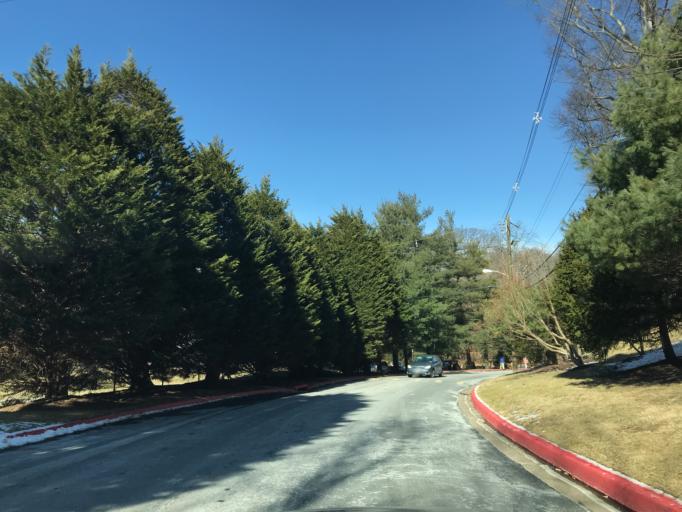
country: US
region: Maryland
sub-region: Baltimore County
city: Towson
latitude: 39.3727
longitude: -76.6342
